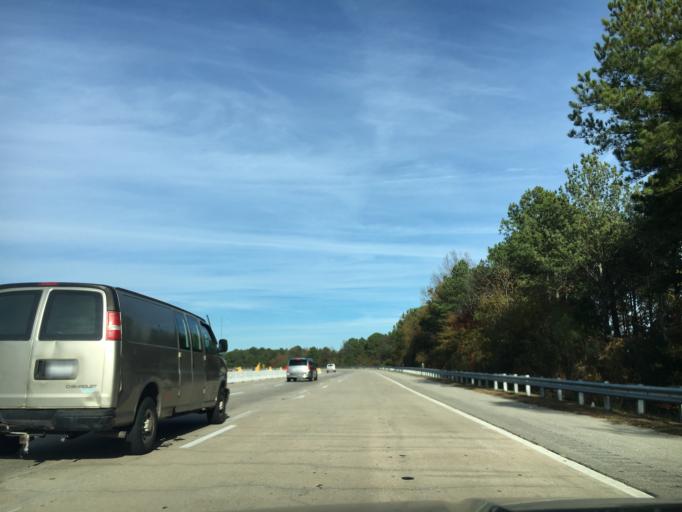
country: US
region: South Carolina
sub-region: Richland County
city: Dentsville
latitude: 34.0906
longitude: -80.9564
